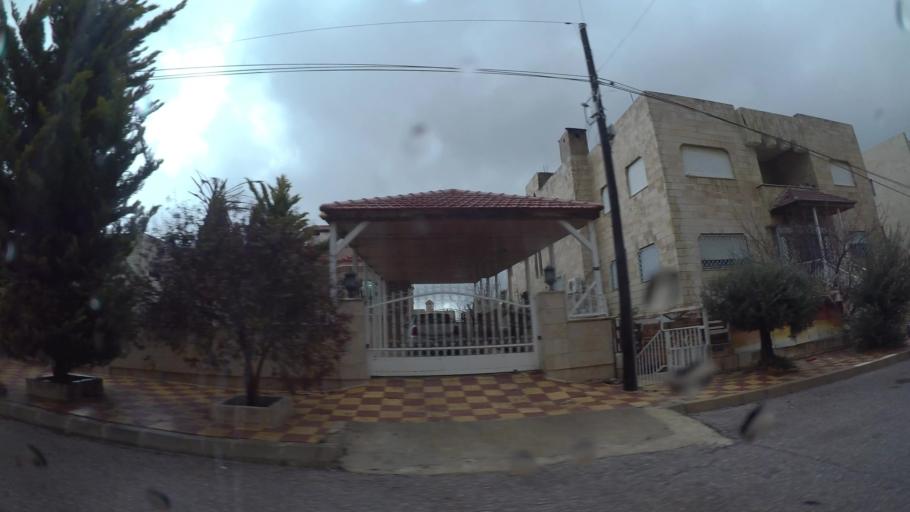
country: JO
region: Amman
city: Al Jubayhah
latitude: 32.0345
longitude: 35.8756
